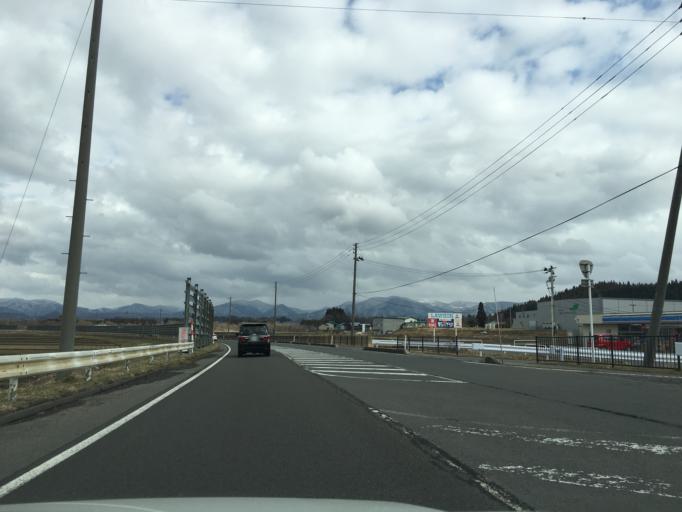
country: JP
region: Akita
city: Hanawa
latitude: 40.2477
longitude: 140.7533
